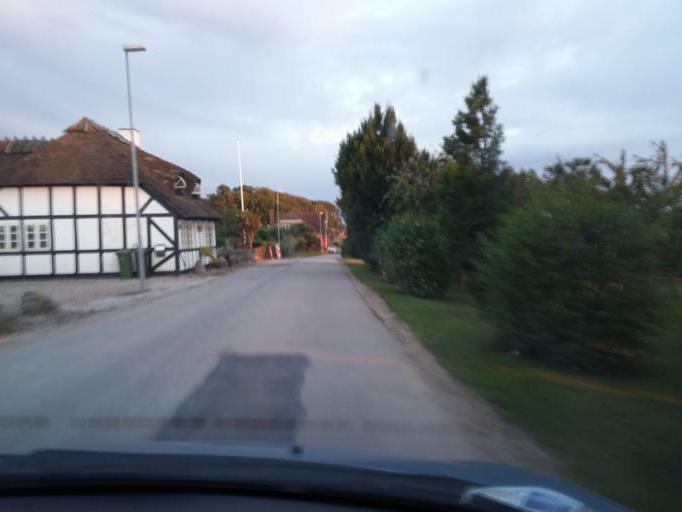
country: DK
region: South Denmark
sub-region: Kerteminde Kommune
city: Munkebo
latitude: 55.4294
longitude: 10.5843
